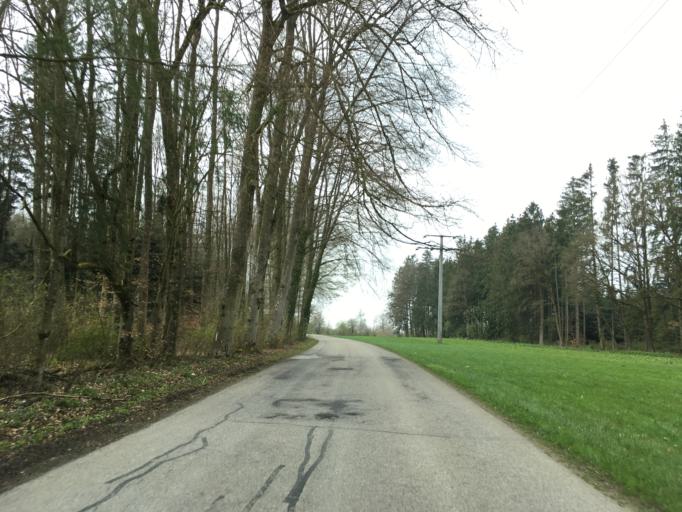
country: DE
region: Bavaria
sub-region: Upper Bavaria
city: Jettenbach
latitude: 48.1596
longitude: 12.3519
